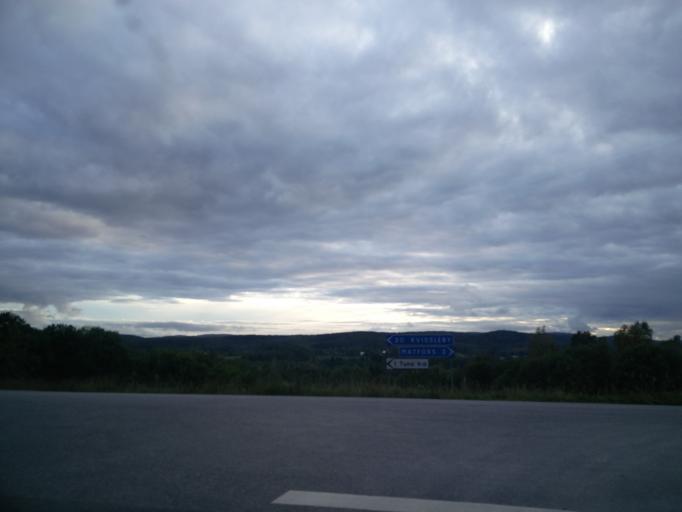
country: SE
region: Vaesternorrland
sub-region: Sundsvalls Kommun
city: Matfors
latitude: 62.3359
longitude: 17.0617
